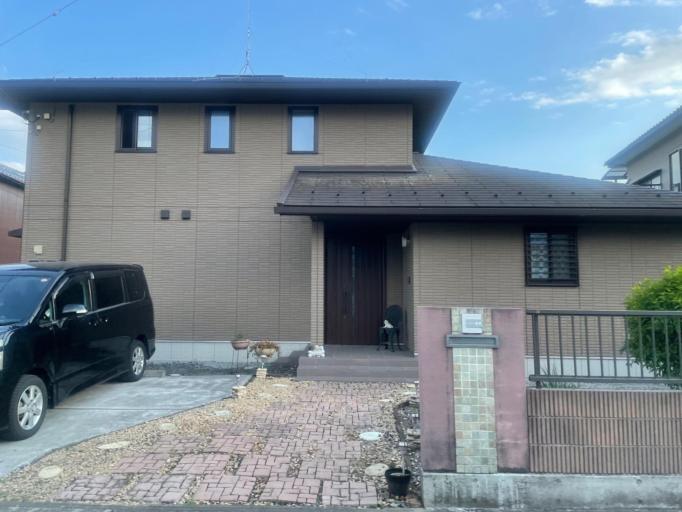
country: JP
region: Tochigi
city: Tochigi
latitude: 36.3743
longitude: 139.7200
